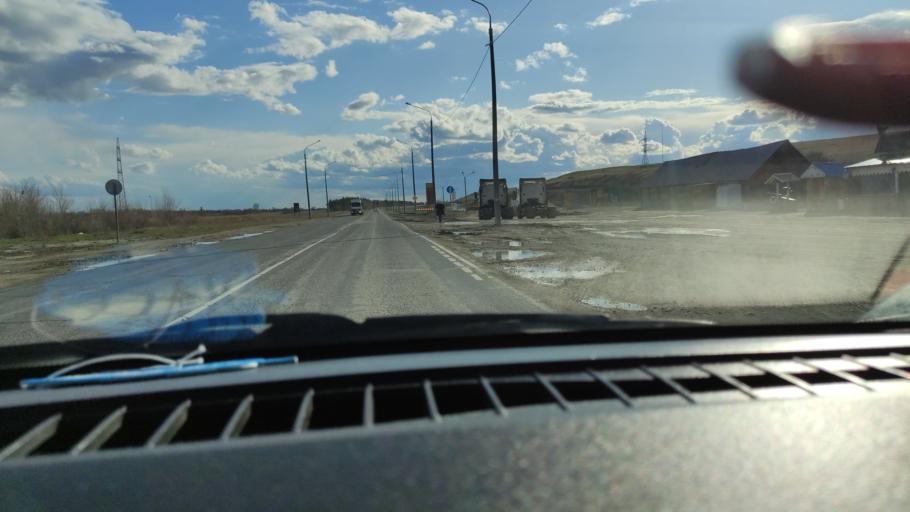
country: RU
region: Saratov
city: Sinodskoye
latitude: 52.0799
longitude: 46.7941
